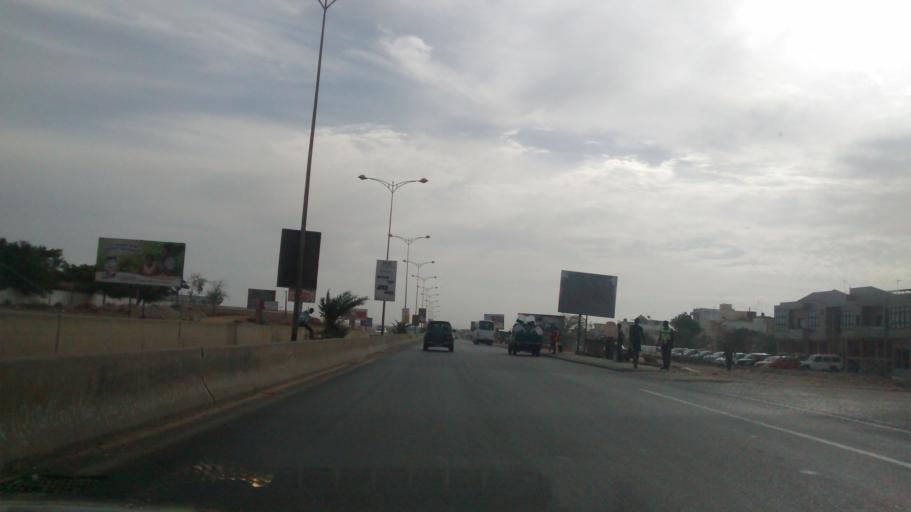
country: SN
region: Dakar
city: Grand Dakar
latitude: 14.7456
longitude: -17.4586
